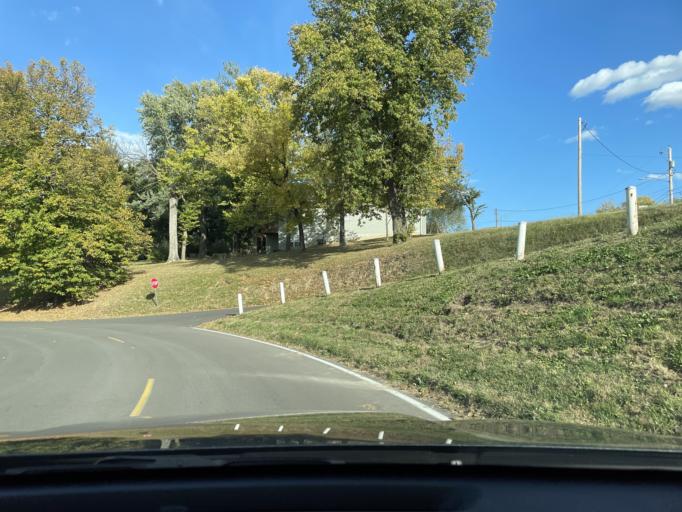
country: US
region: Kansas
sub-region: Doniphan County
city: Elwood
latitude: 39.7193
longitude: -94.8461
